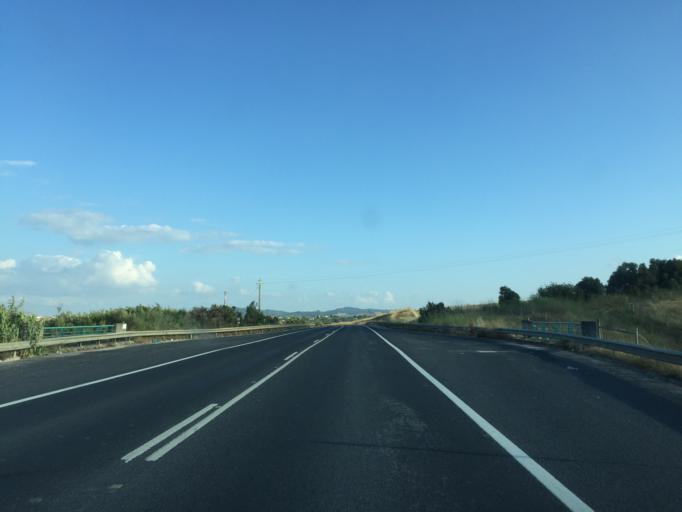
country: PT
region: Lisbon
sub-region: Alenquer
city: Alenquer
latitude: 39.0583
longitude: -8.9957
